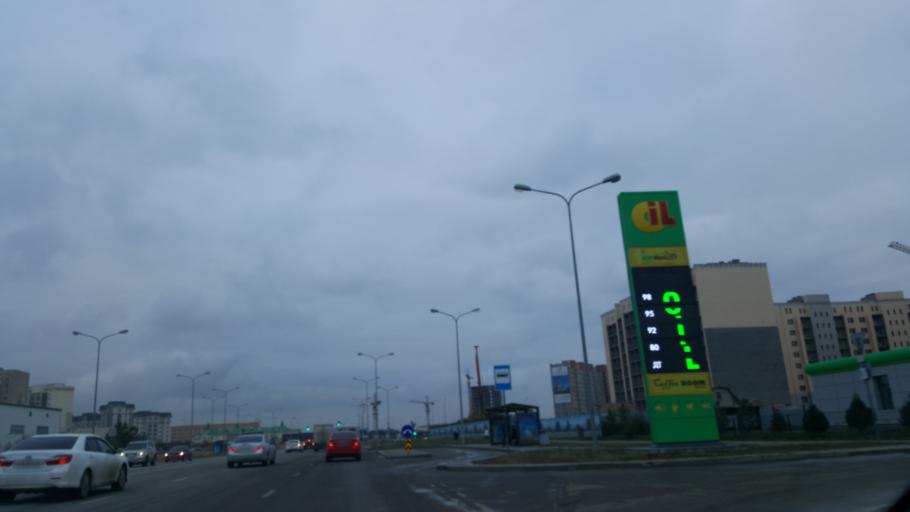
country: KZ
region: Astana Qalasy
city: Astana
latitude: 51.1281
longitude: 71.4852
